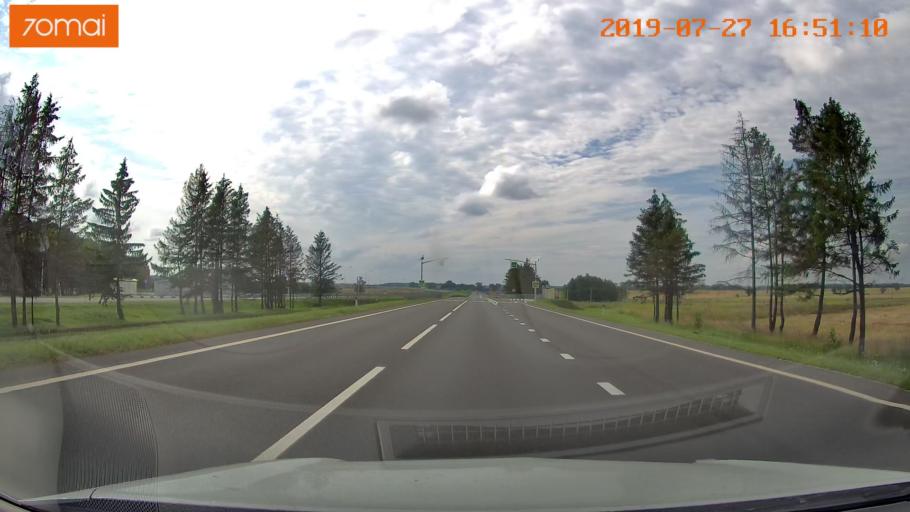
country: RU
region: Kaliningrad
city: Gvardeysk
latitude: 54.6813
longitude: 20.8943
